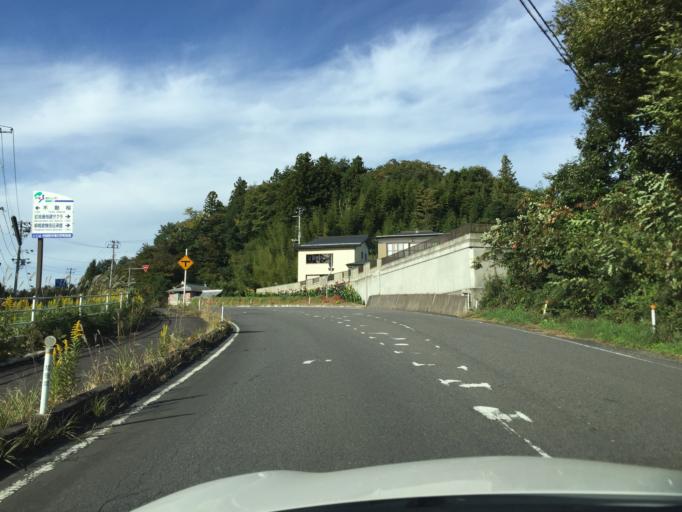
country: JP
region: Fukushima
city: Miharu
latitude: 37.3572
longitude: 140.5149
